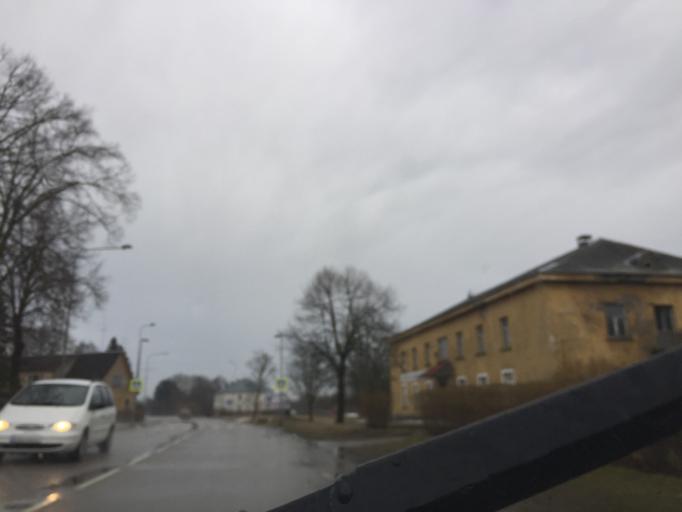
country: EE
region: Saare
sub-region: Orissaare vald
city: Orissaare
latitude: 58.5588
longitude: 23.0841
